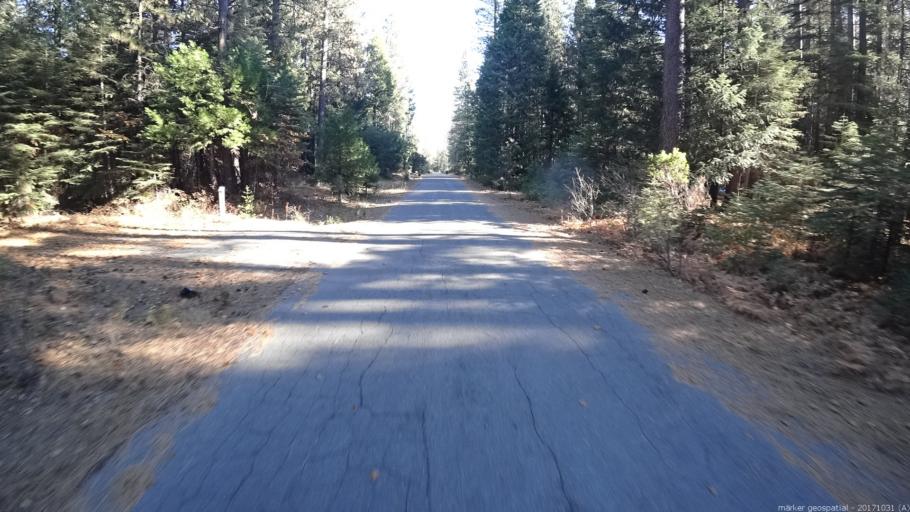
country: US
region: California
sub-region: Shasta County
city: Shingletown
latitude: 40.5105
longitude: -121.8248
